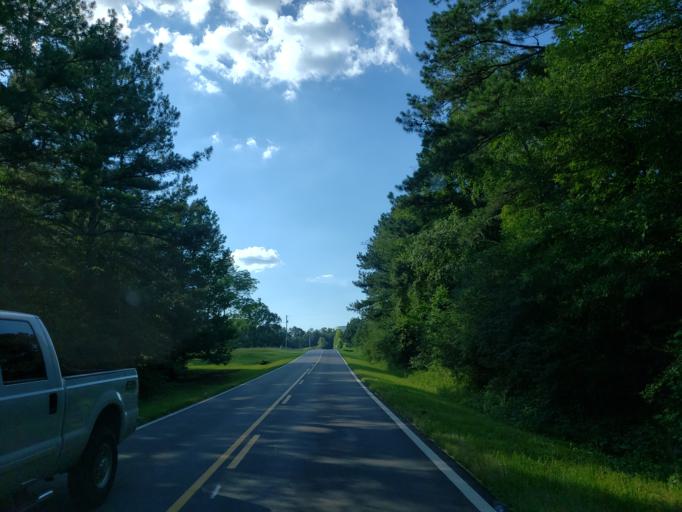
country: US
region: Georgia
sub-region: Haralson County
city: Bremen
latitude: 33.6879
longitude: -85.1338
